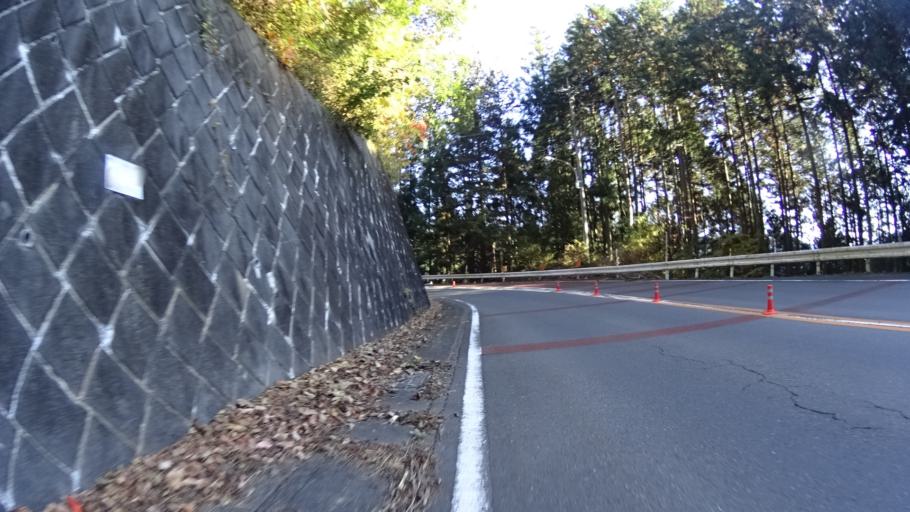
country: JP
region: Yamanashi
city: Uenohara
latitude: 35.6995
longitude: 139.1034
